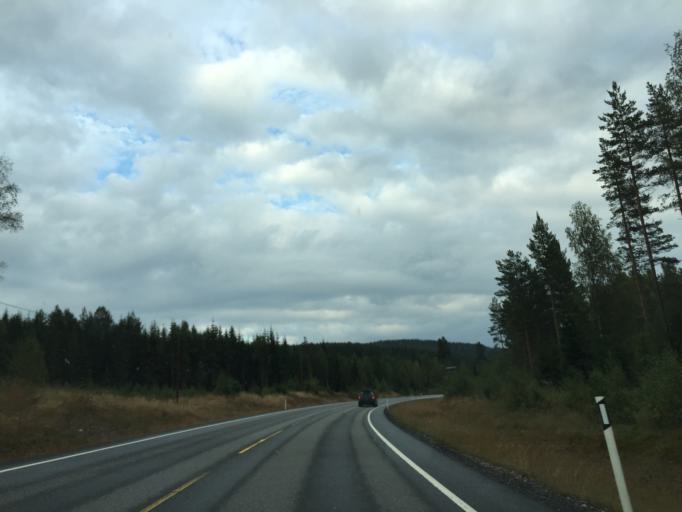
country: NO
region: Hedmark
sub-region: Nord-Odal
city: Sand
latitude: 60.5792
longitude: 11.4979
